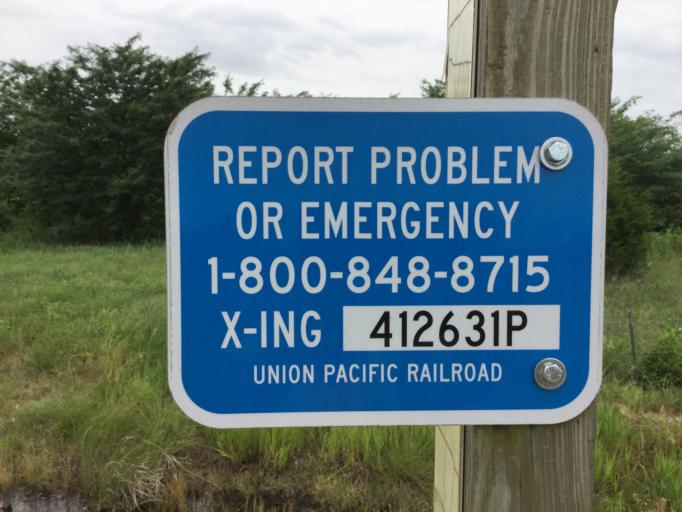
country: US
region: Kansas
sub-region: Anderson County
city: Garnett
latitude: 38.1981
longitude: -95.0400
